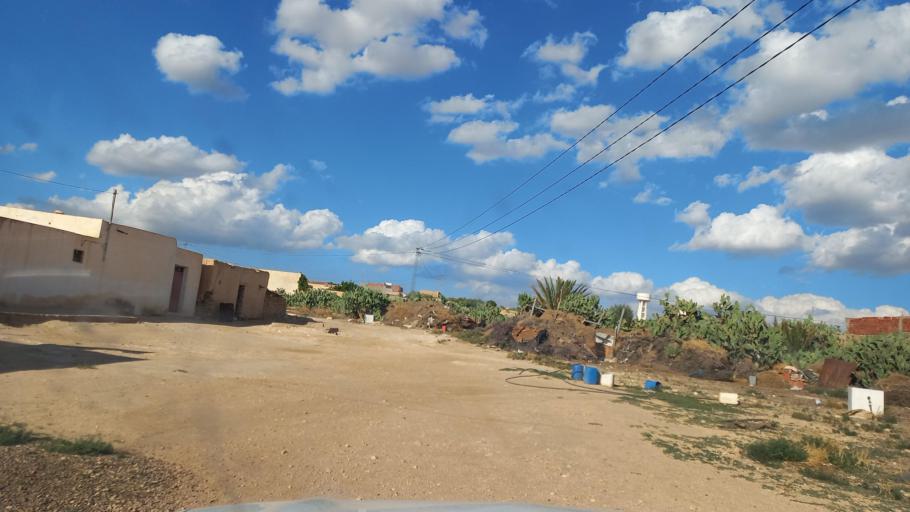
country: TN
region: Al Qasrayn
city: Sbiba
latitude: 35.3882
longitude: 9.0424
